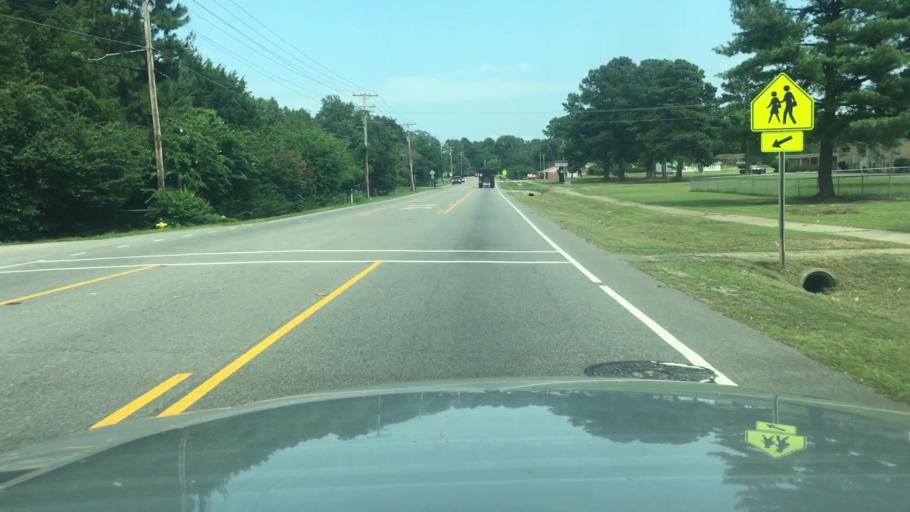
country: US
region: North Carolina
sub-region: Cumberland County
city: Fayetteville
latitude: 35.1216
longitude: -78.9108
